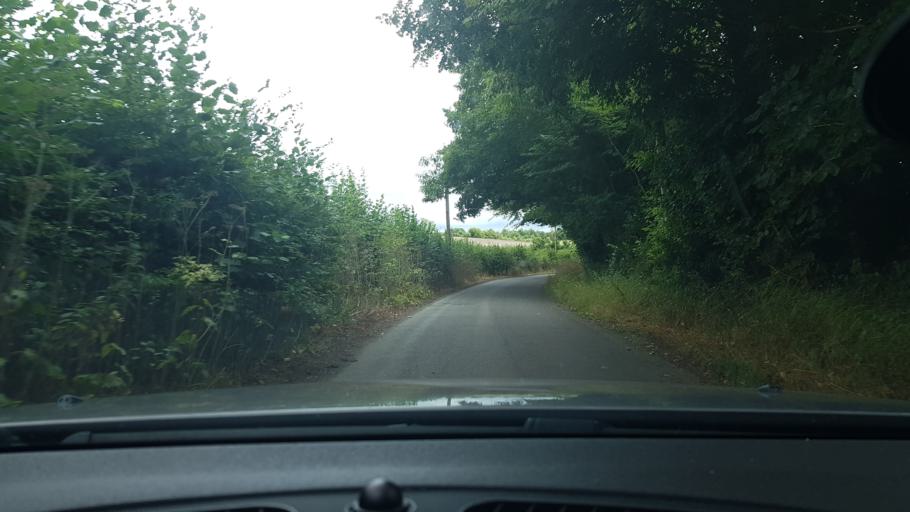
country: GB
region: England
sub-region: West Berkshire
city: Hungerford
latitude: 51.4432
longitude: -1.5070
